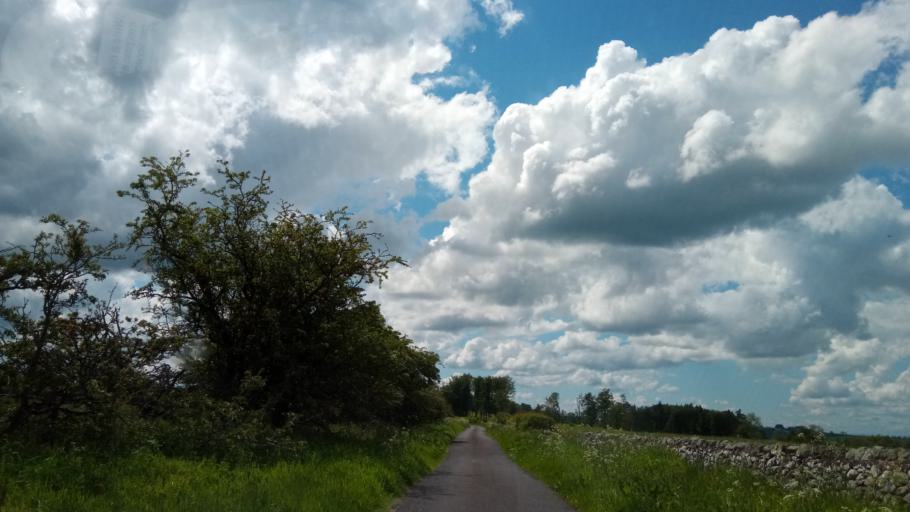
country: GB
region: Scotland
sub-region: The Scottish Borders
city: Coldstream
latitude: 55.5951
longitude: -2.2825
